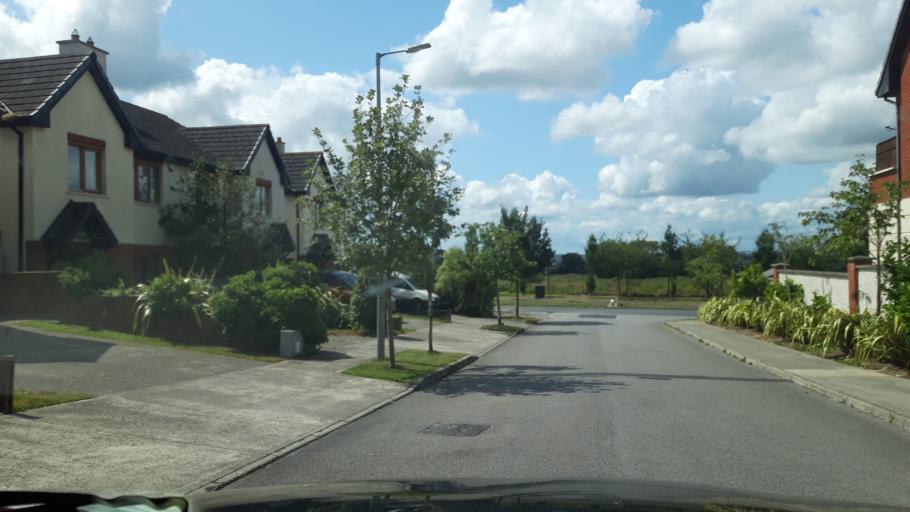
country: IE
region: Munster
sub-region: Waterford
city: Waterford
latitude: 52.2694
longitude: -7.0858
